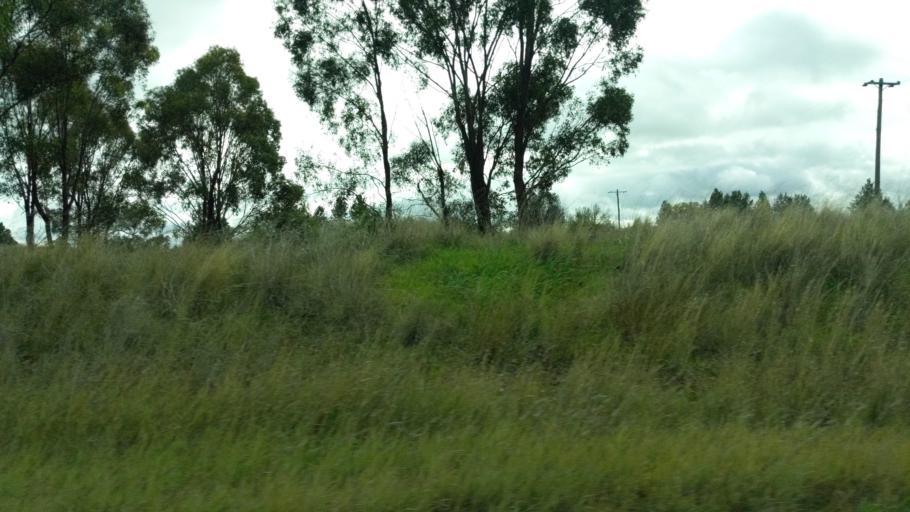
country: AU
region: New South Wales
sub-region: Narrandera
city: Narrandera
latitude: -34.7425
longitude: 146.7950
